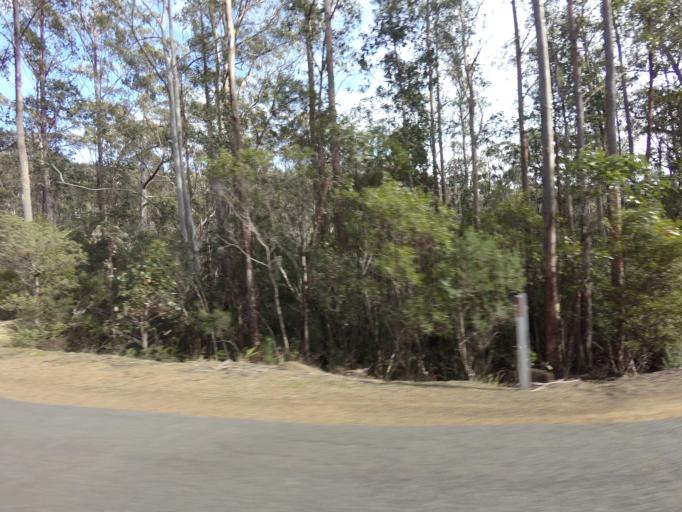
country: AU
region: Tasmania
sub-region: Kingborough
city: Margate
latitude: -43.0051
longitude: 147.1704
